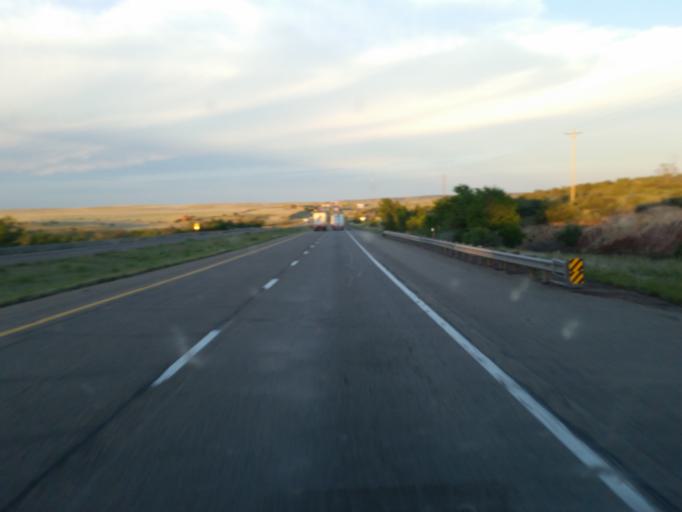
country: US
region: New Mexico
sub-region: San Miguel County
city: Las Vegas
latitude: 34.9924
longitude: -105.3143
